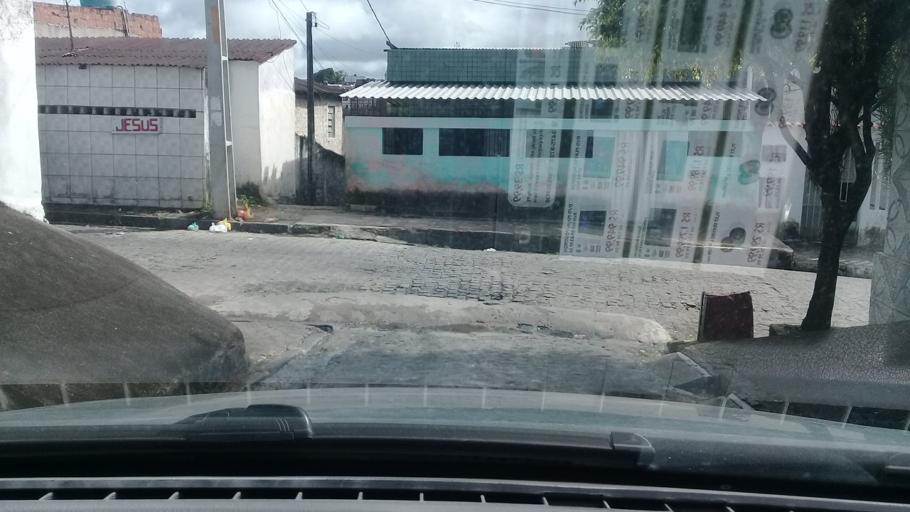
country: BR
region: Pernambuco
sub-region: Jaboatao Dos Guararapes
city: Jaboatao dos Guararapes
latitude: -8.1198
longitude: -34.9492
